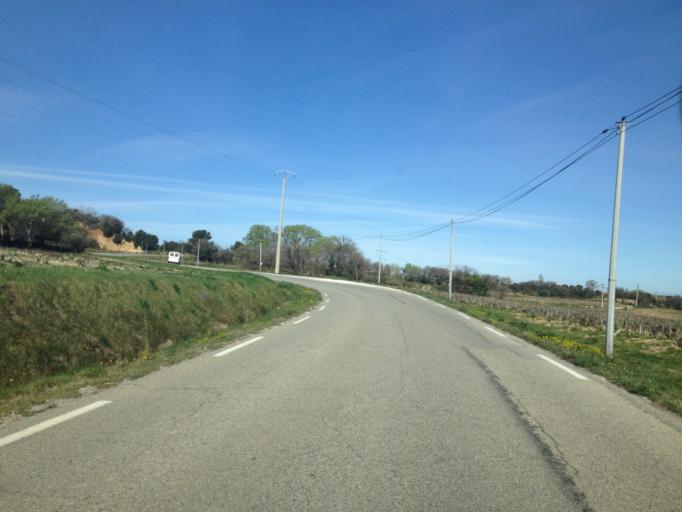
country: FR
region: Provence-Alpes-Cote d'Azur
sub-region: Departement du Vaucluse
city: Bedarrides
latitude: 44.0476
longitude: 4.8797
